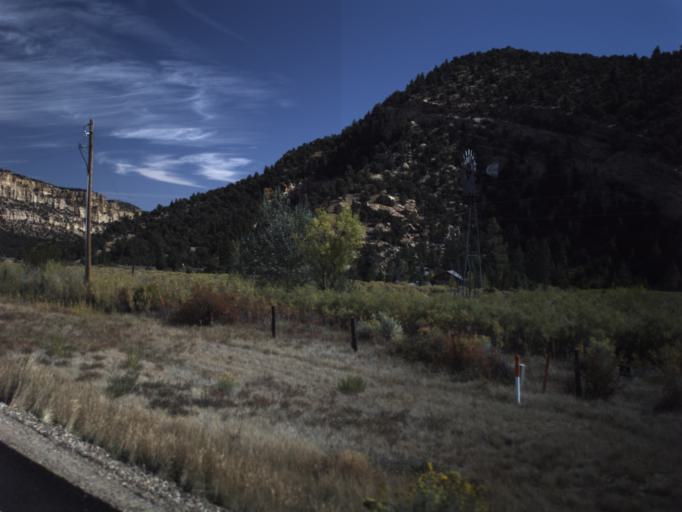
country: US
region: Utah
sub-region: Garfield County
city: Panguitch
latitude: 37.7188
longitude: -111.7820
